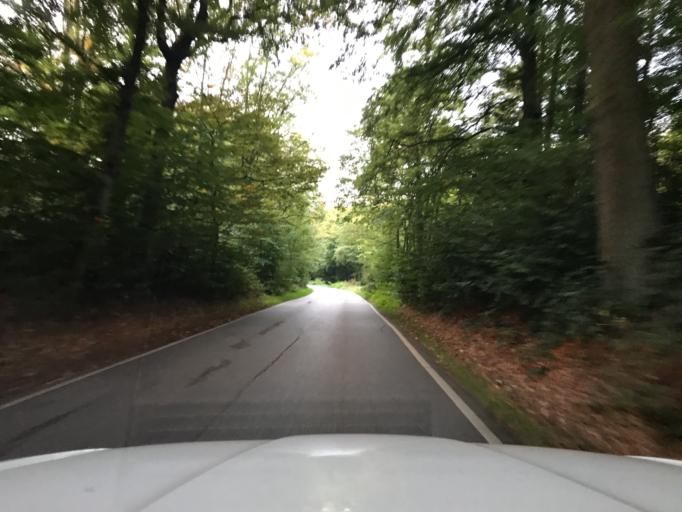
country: DE
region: North Rhine-Westphalia
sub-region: Regierungsbezirk Dusseldorf
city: Duisburg
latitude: 51.4034
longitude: 6.8156
